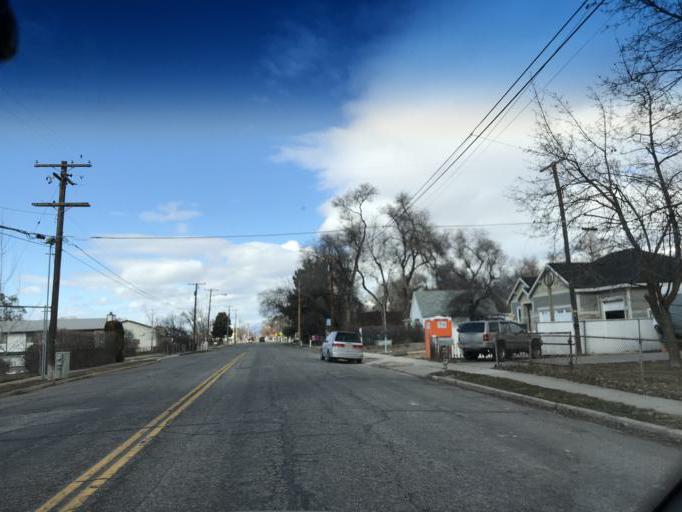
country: US
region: Utah
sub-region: Davis County
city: Woods Cross
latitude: 40.8717
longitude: -111.9021
